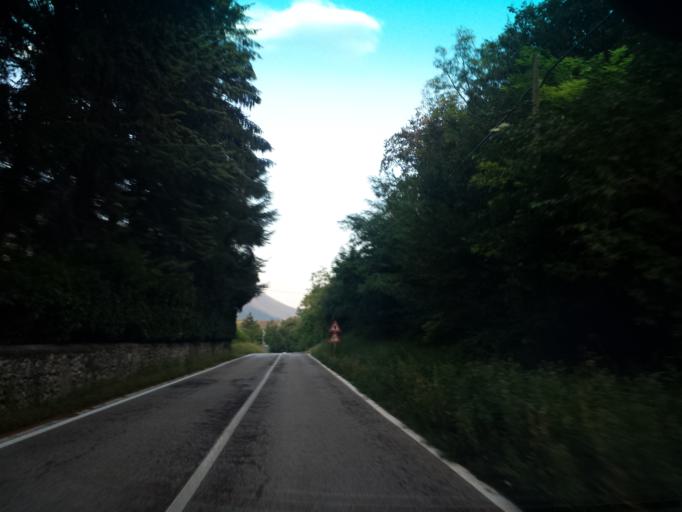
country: IT
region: Veneto
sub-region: Provincia di Vicenza
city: Velo d'Astico
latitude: 45.7834
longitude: 11.3897
